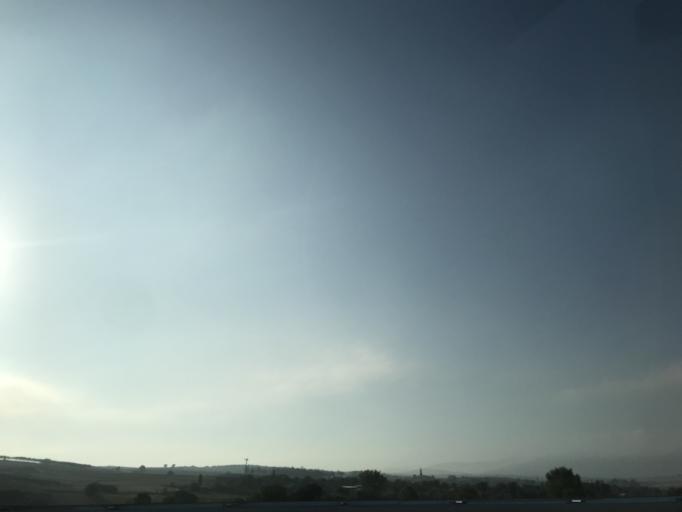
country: TR
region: Balikesir
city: Gobel
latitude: 40.0253
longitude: 28.2088
